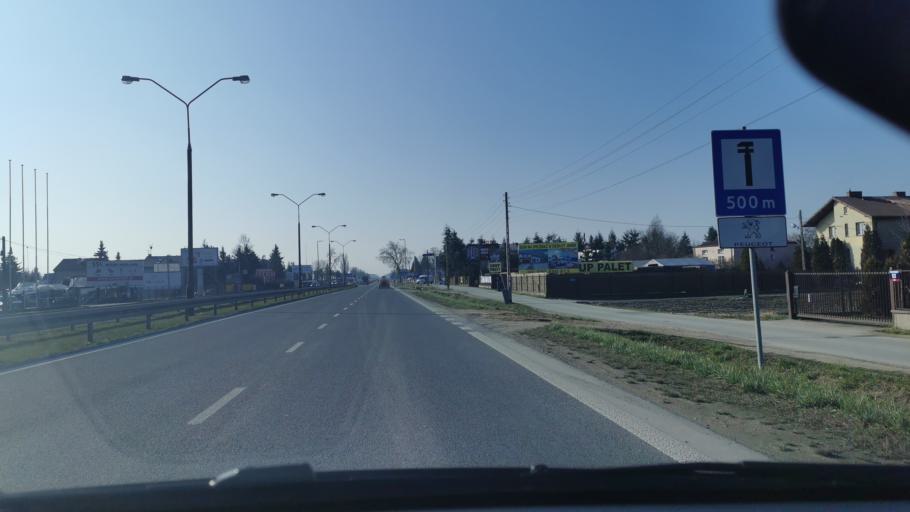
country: PL
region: Masovian Voivodeship
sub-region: Powiat pruszkowski
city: Nowe Grocholice
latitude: 52.1267
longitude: 20.8957
